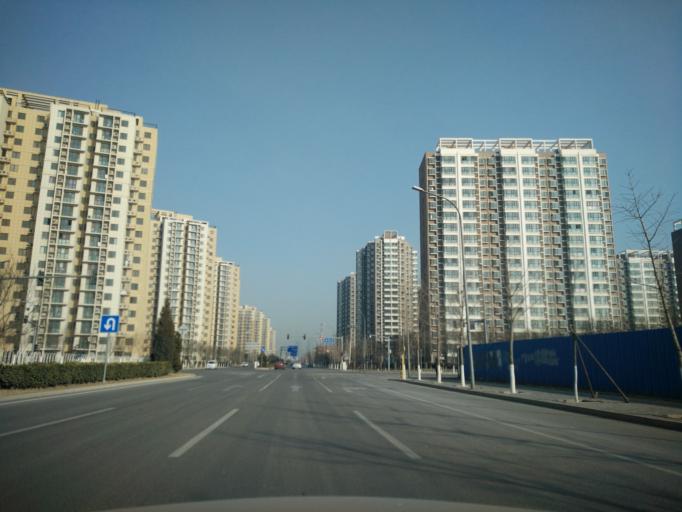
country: CN
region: Beijing
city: Yinghai
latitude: 39.7535
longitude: 116.4901
